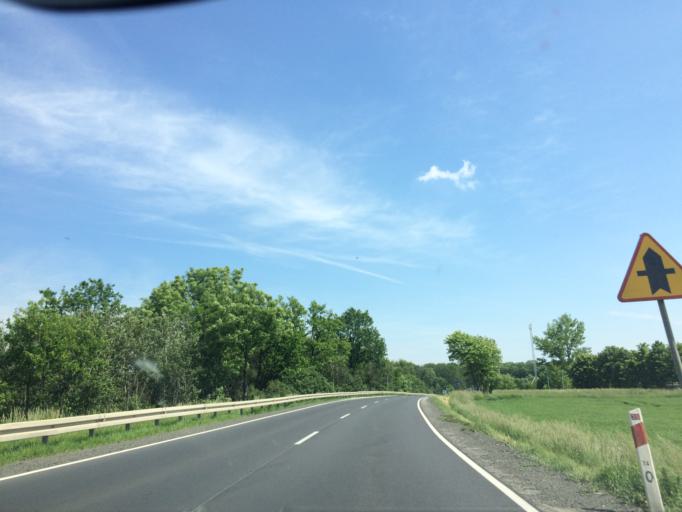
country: PL
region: Lower Silesian Voivodeship
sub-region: Powiat wroclawski
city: Gniechowice
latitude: 50.9819
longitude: 16.8184
